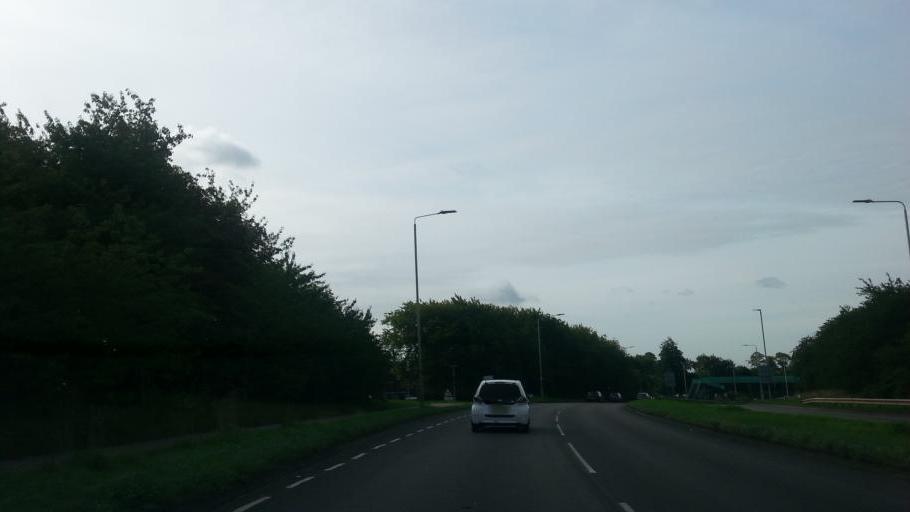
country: GB
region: England
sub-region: Leicestershire
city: Syston
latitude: 52.6824
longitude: -1.0925
